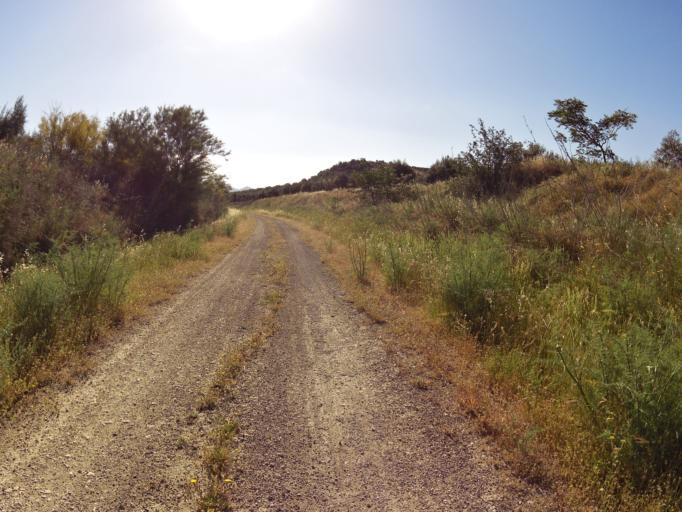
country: ES
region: Andalusia
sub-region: Province of Cordoba
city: Fuente-Tojar
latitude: 37.5819
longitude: -4.1957
